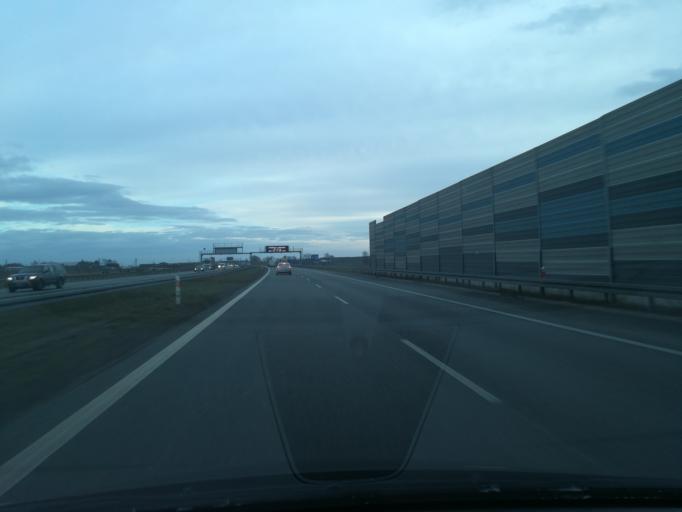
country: PL
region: Lodz Voivodeship
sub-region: Powiat leczycki
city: Piatek
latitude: 52.0551
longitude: 19.5353
